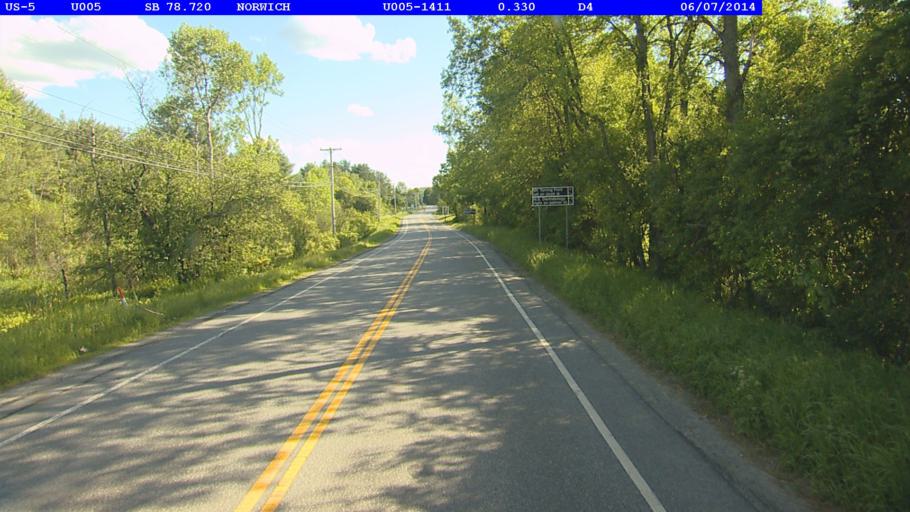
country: US
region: New Hampshire
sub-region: Grafton County
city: Hanover
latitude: 43.7005
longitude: -72.3160
